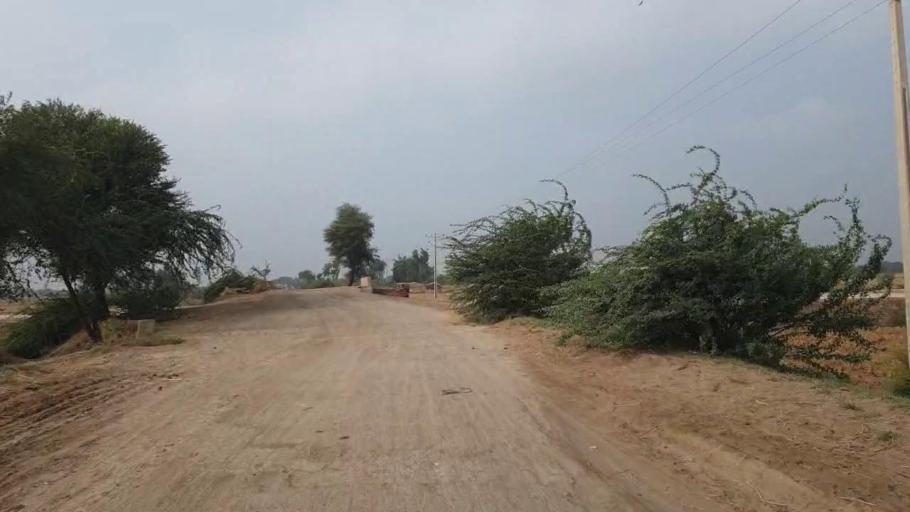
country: PK
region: Sindh
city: Matli
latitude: 24.9639
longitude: 68.5903
